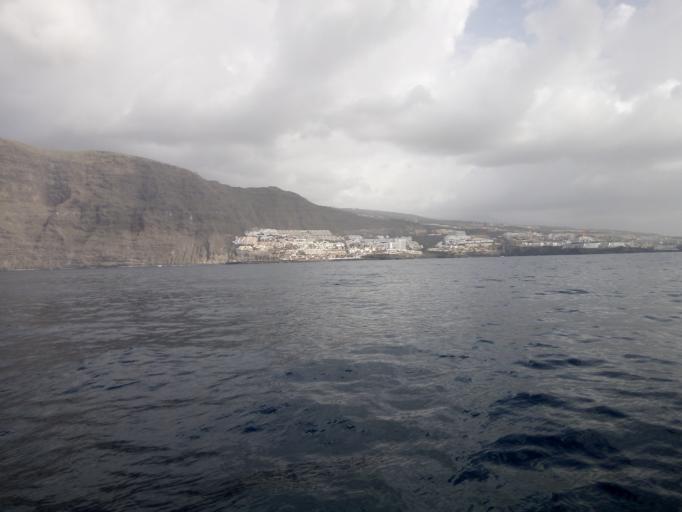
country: ES
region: Canary Islands
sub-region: Provincia de Santa Cruz de Tenerife
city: Santiago del Teide
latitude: 28.2502
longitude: -16.8577
